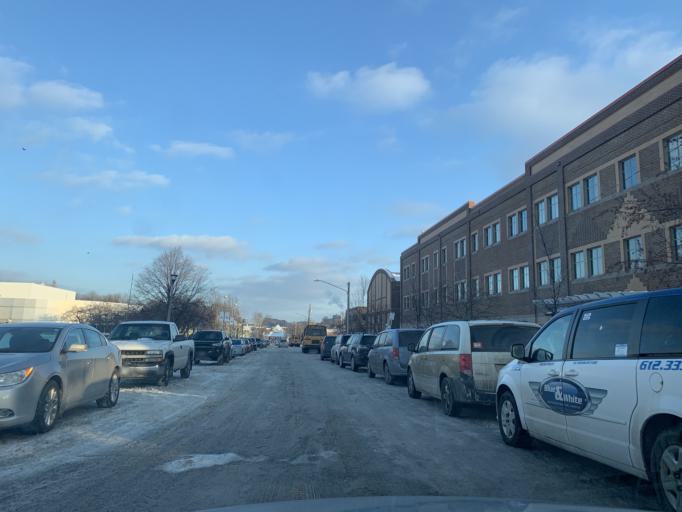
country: US
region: Minnesota
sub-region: Hennepin County
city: Minneapolis
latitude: 44.9852
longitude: -93.2981
